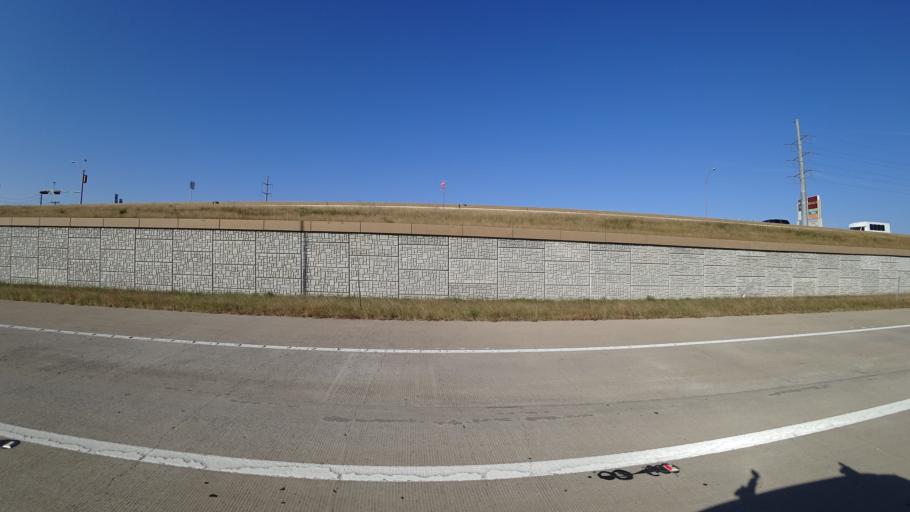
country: US
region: Texas
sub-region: Travis County
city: Pflugerville
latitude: 30.4656
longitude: -97.5948
